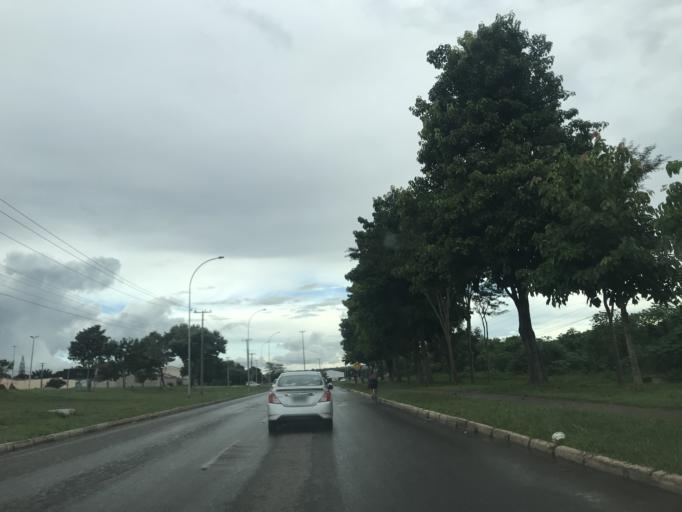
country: BR
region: Federal District
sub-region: Brasilia
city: Brasilia
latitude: -15.6444
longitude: -47.8110
